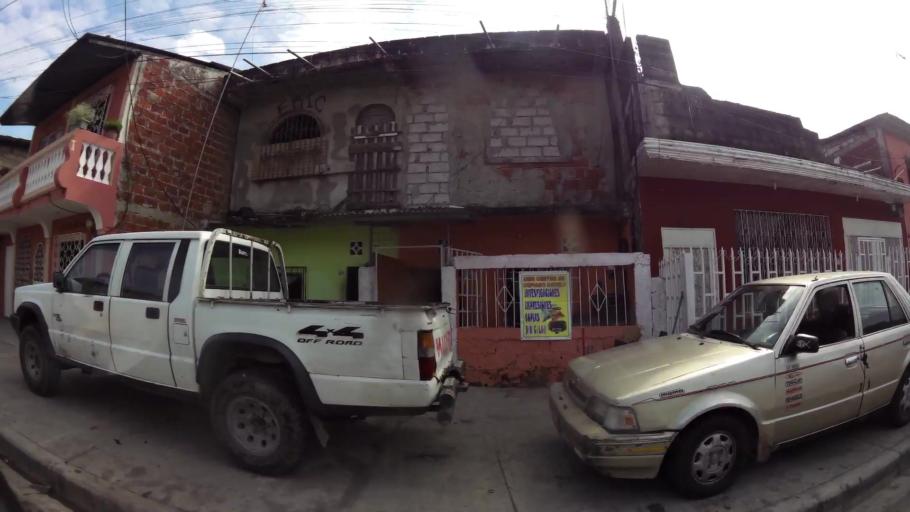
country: EC
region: Guayas
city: Guayaquil
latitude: -2.2594
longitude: -79.8819
